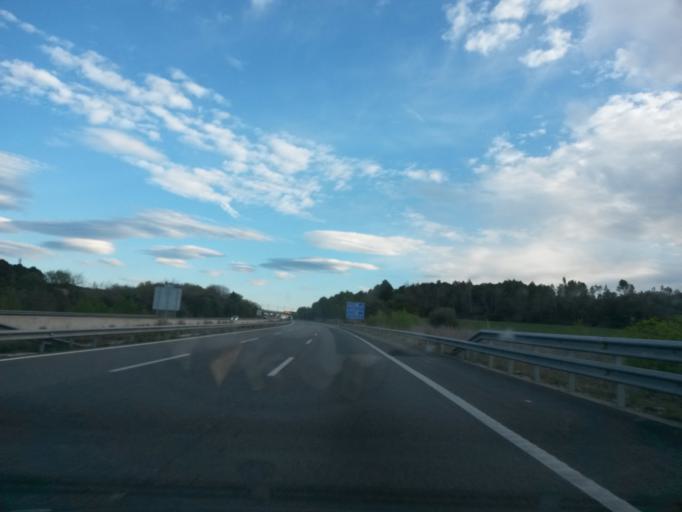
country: ES
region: Catalonia
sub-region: Provincia de Girona
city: Pontos
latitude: 42.1817
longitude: 2.9336
